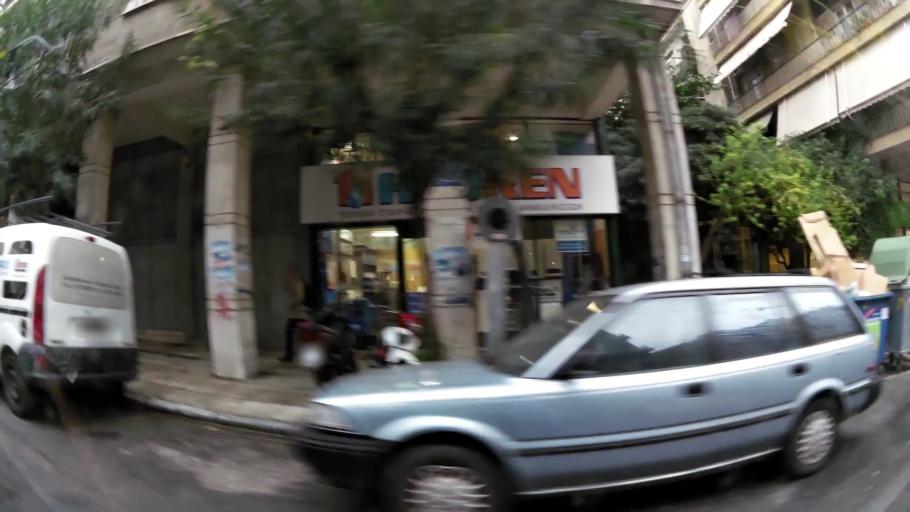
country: GR
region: Attica
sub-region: Nomarchia Athinas
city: Vyronas
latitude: 37.9692
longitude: 23.7431
